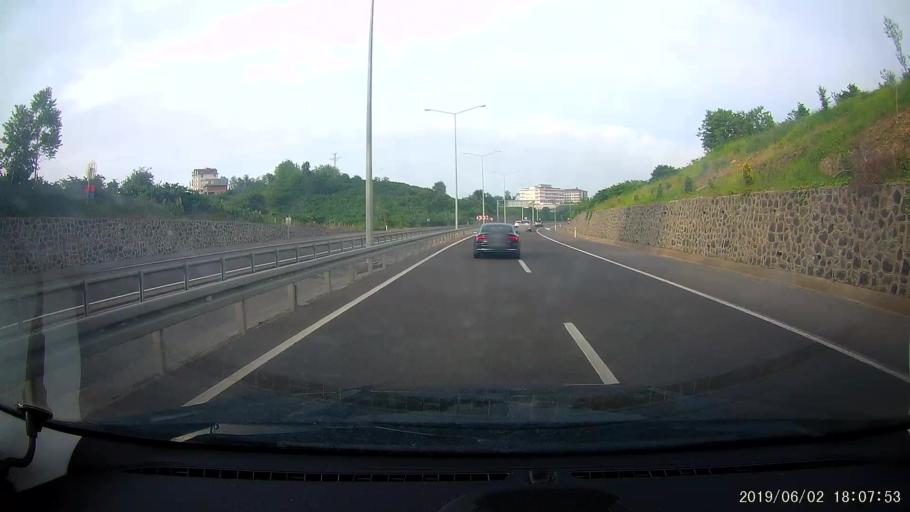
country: TR
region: Ordu
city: Unieh
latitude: 41.1147
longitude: 37.2942
